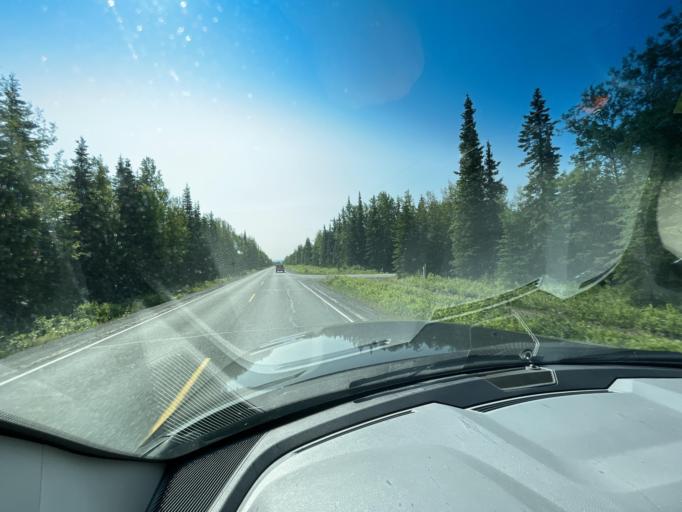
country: US
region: Alaska
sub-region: Kenai Peninsula Borough
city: Cohoe
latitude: 60.3086
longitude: -151.2899
